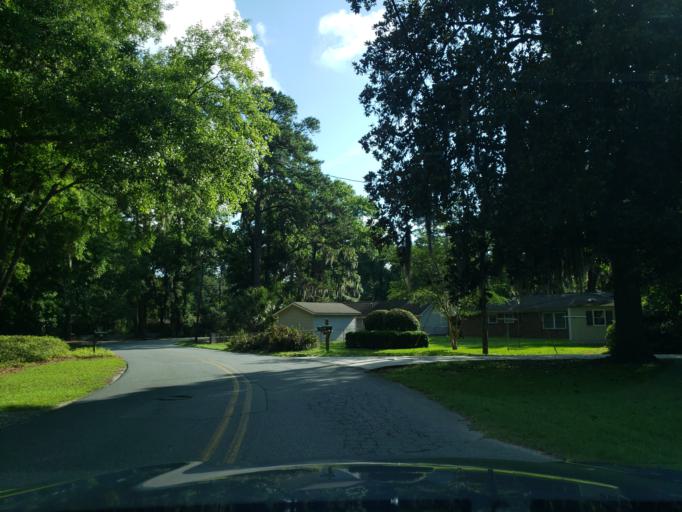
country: US
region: Georgia
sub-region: Chatham County
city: Isle of Hope
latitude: 31.9848
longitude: -81.0567
